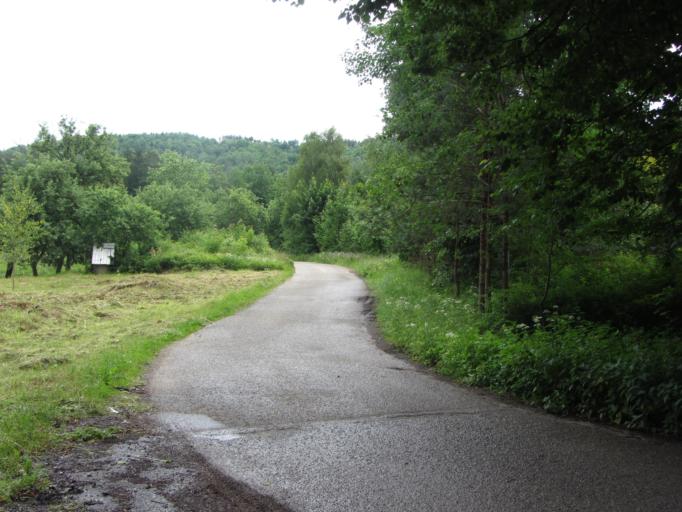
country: LT
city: Grigiskes
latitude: 54.7152
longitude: 25.0561
